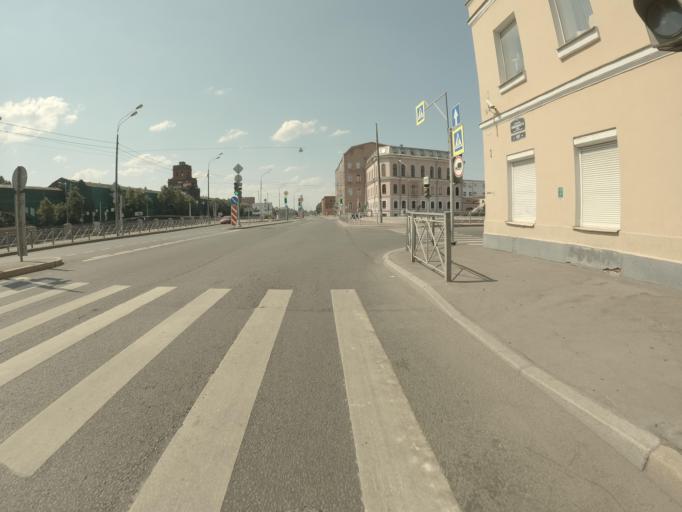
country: RU
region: St.-Petersburg
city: Admiralteisky
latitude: 59.9094
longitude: 30.2888
